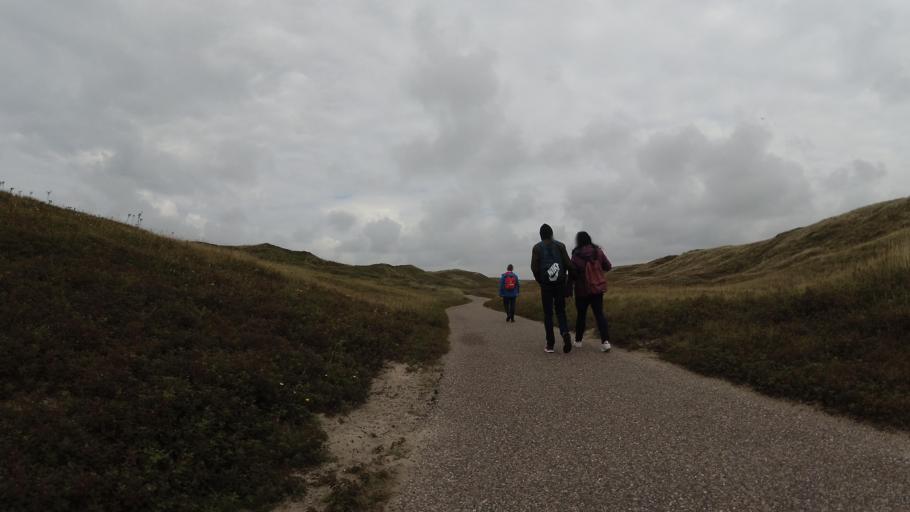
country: NL
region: North Holland
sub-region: Gemeente Den Helder
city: Den Helder
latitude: 52.9072
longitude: 4.7171
